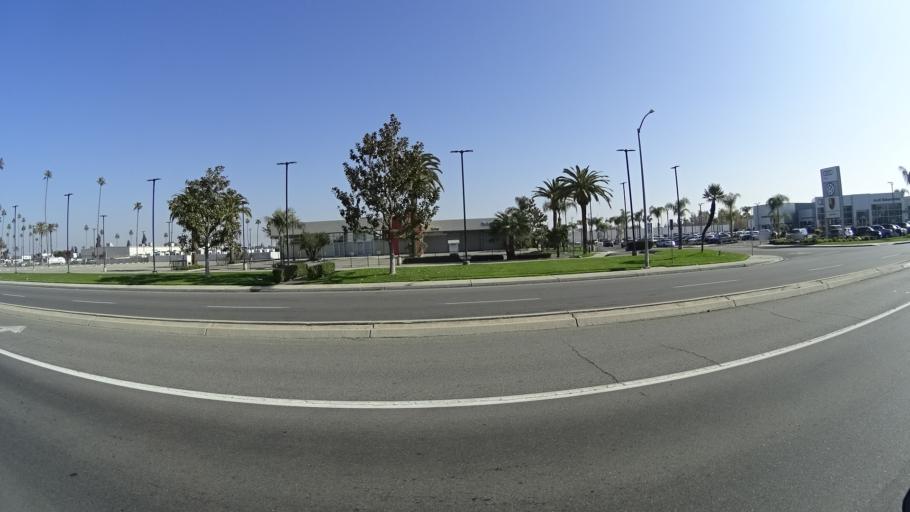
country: US
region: California
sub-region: Kern County
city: Greenfield
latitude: 35.3015
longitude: -119.0391
